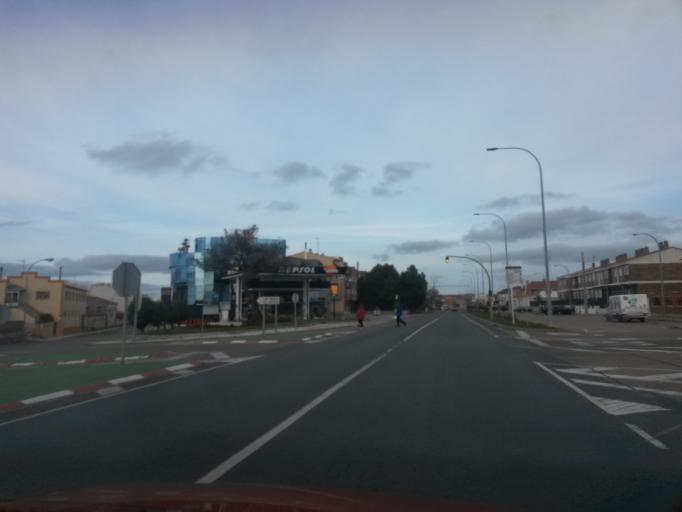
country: ES
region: Castille and Leon
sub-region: Provincia de Salamanca
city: Villares de la Reina
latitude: 41.0041
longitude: -5.6496
